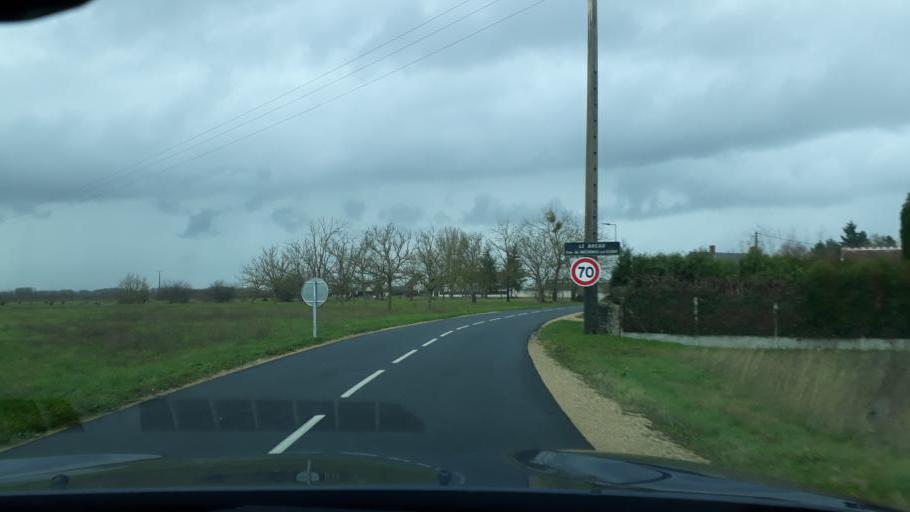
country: FR
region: Centre
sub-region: Departement du Loiret
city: Mareau-aux-Pres
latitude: 47.8317
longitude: 1.7976
